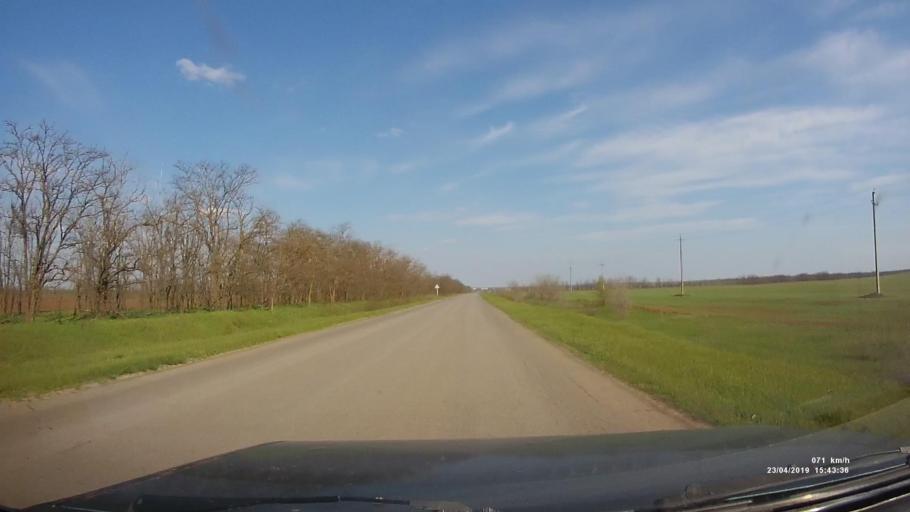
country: RU
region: Rostov
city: Remontnoye
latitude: 46.5444
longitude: 43.0849
